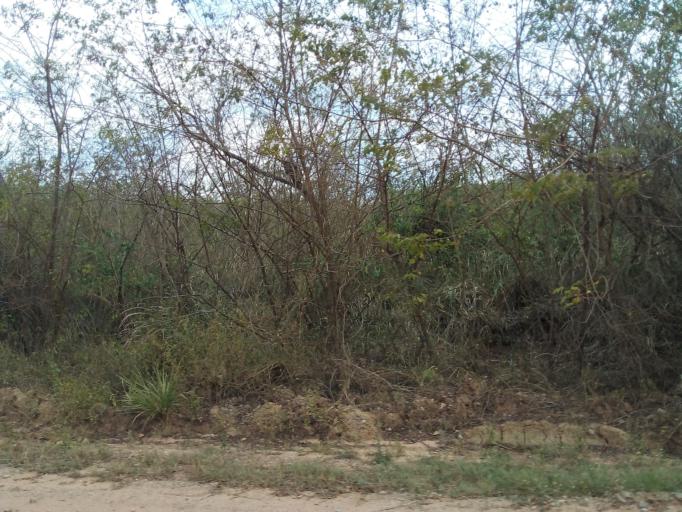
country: BR
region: Maranhao
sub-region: Icatu
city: Icatu
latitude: -2.9270
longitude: -44.3481
